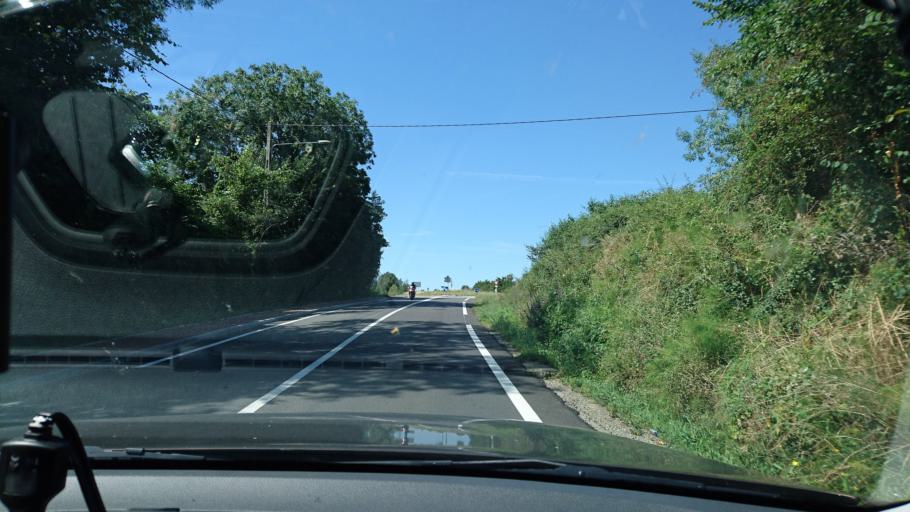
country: FR
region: Midi-Pyrenees
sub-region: Departement de la Haute-Garonne
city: Longages
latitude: 43.3397
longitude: 1.2579
